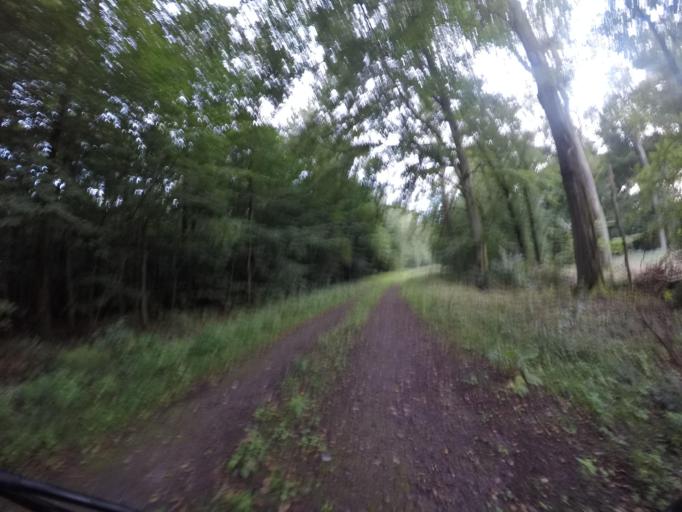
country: DE
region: Lower Saxony
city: Neu Darchau
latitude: 53.2755
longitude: 10.8914
